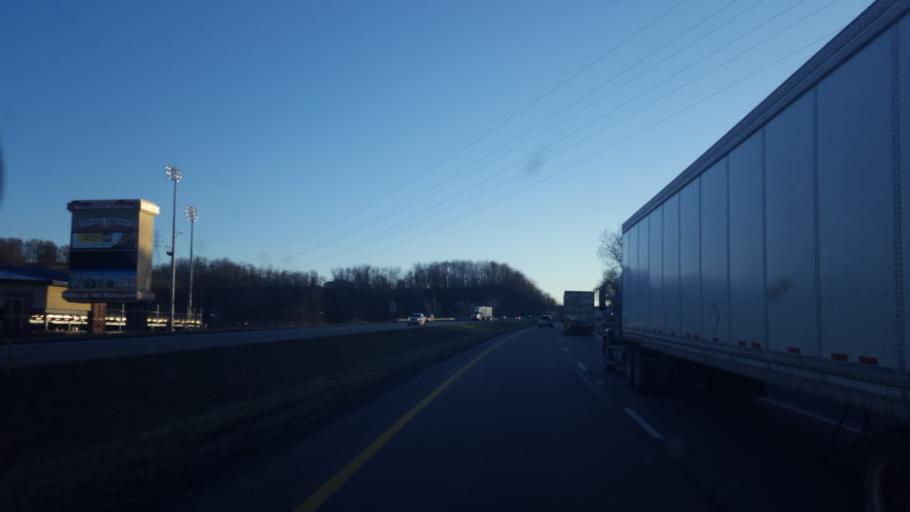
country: US
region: Pennsylvania
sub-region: Washington County
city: Wolfdale
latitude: 40.1560
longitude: -80.2836
